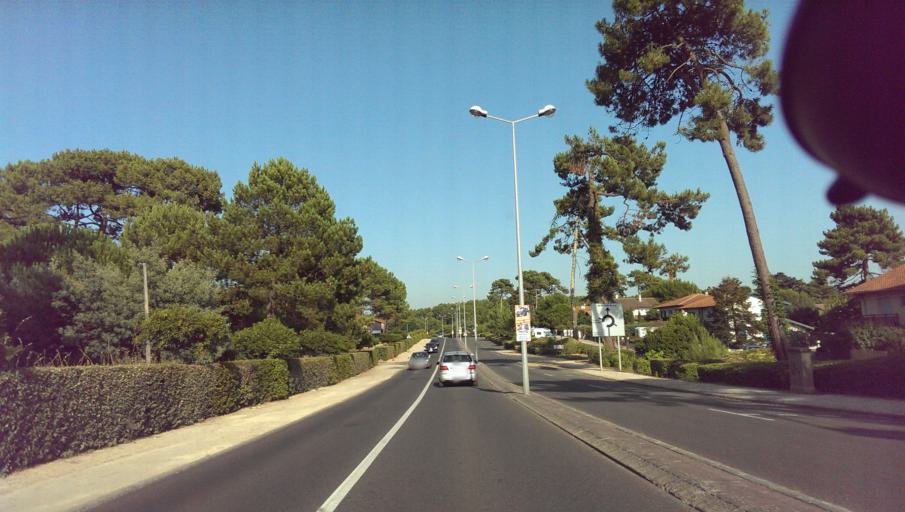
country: FR
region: Aquitaine
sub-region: Departement des Landes
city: Mimizan
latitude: 44.2118
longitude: -1.2875
